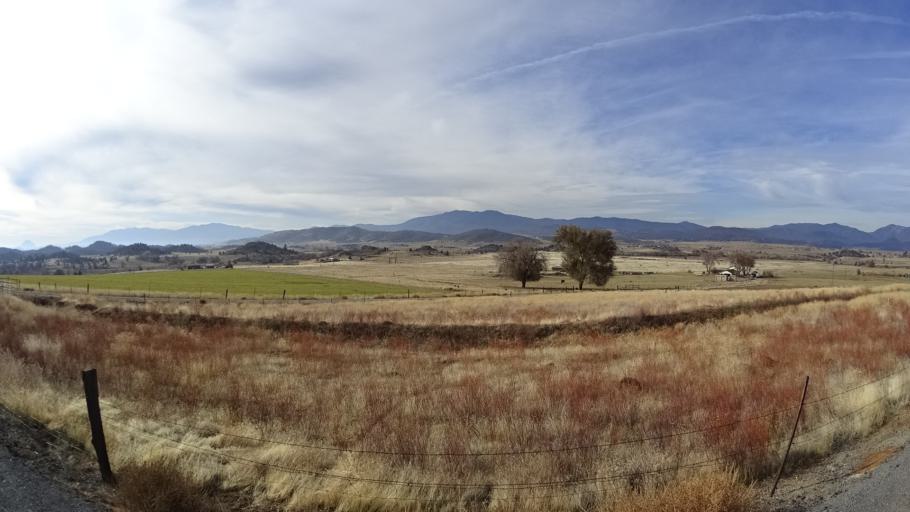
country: US
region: California
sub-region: Siskiyou County
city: Montague
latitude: 41.7098
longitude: -122.5193
